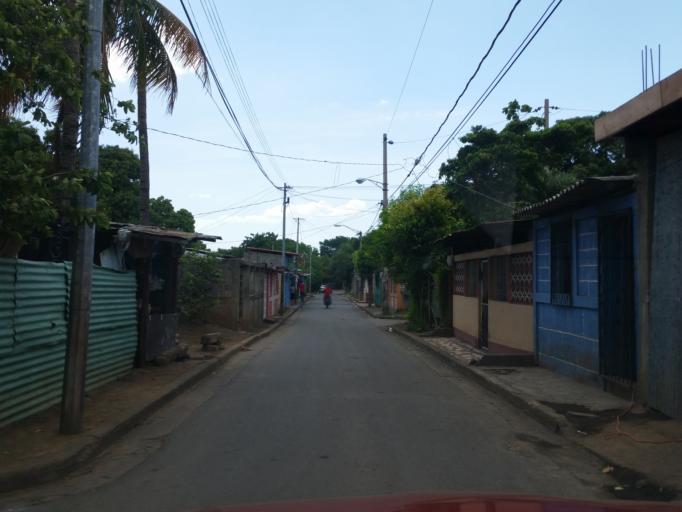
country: NI
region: Managua
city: Managua
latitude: 12.1273
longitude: -86.2463
